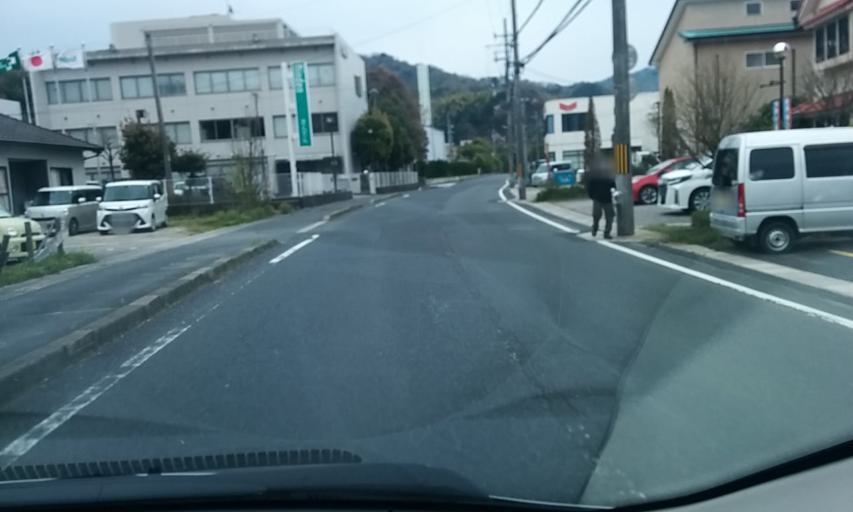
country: JP
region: Kyoto
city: Miyazu
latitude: 35.5520
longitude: 135.2106
